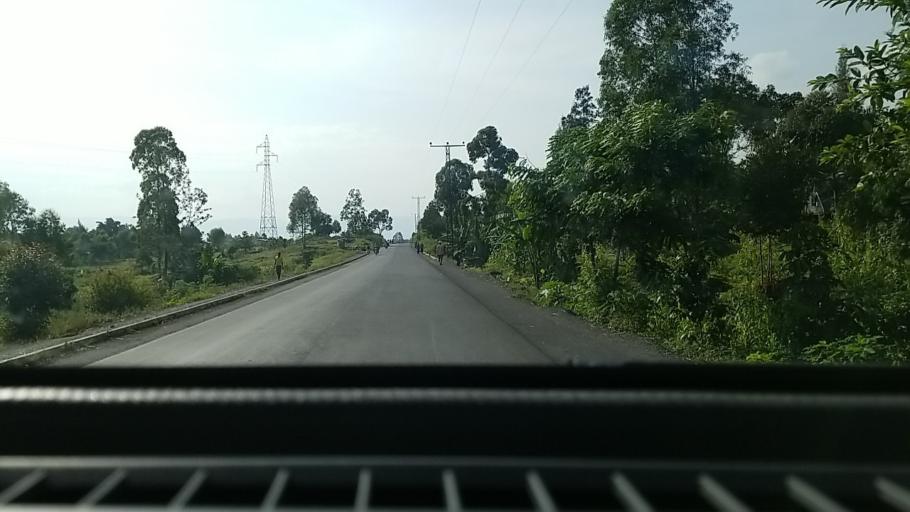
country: CD
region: Nord Kivu
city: Sake
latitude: -1.6076
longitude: 29.1333
